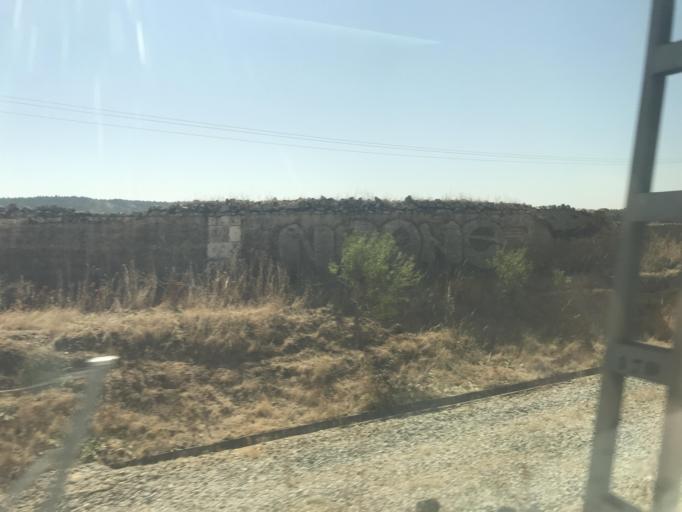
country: ES
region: Castille and Leon
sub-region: Provincia de Palencia
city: Venta de Banos
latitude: 41.9046
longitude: -4.5113
